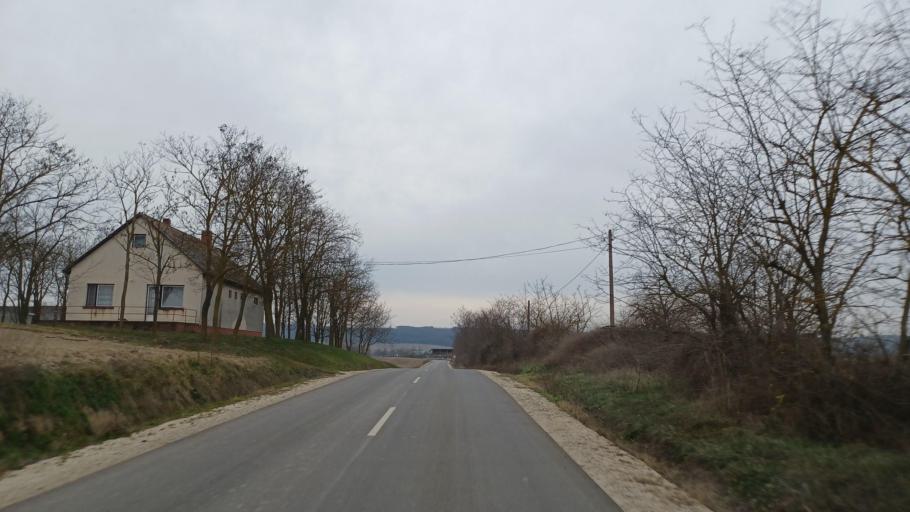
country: HU
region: Tolna
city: Nagydorog
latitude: 46.5635
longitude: 18.6130
